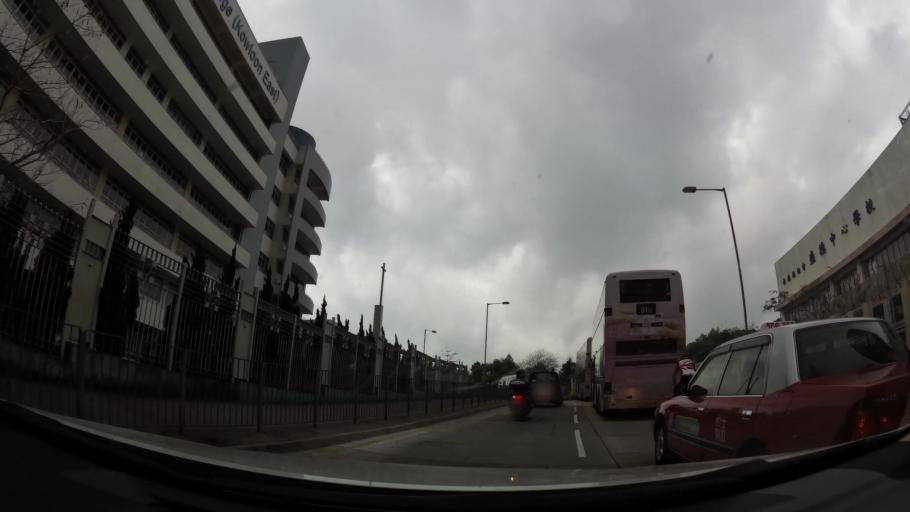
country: HK
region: Kowloon City
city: Kowloon
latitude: 22.3312
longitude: 114.2222
